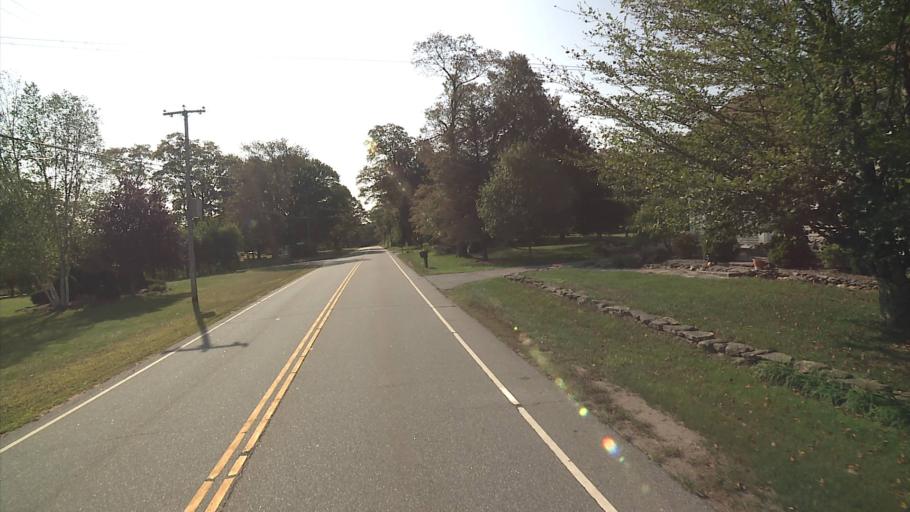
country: US
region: Connecticut
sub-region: Windham County
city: Willimantic
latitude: 41.6800
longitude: -72.2764
